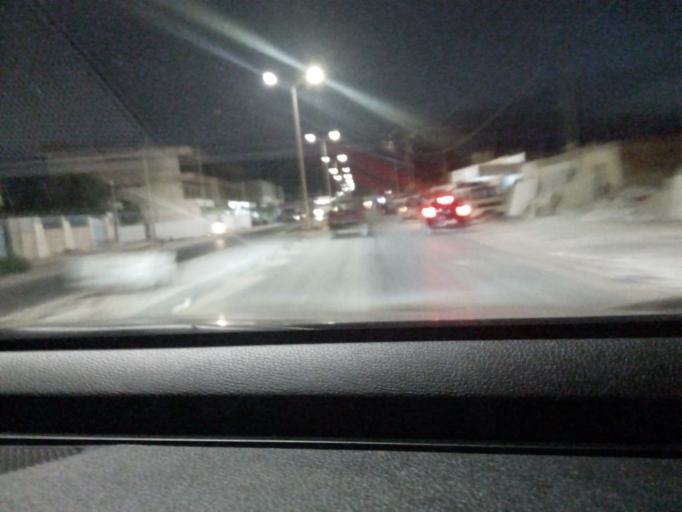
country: TN
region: Safaqis
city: Sfax
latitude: 34.7311
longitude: 10.6665
